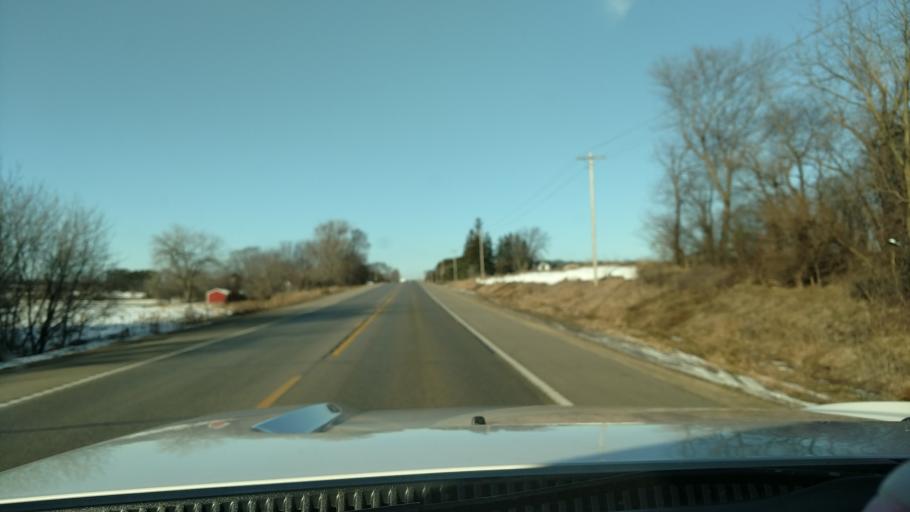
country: US
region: Minnesota
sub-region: Olmsted County
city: Oronoco
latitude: 44.1082
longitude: -92.4927
